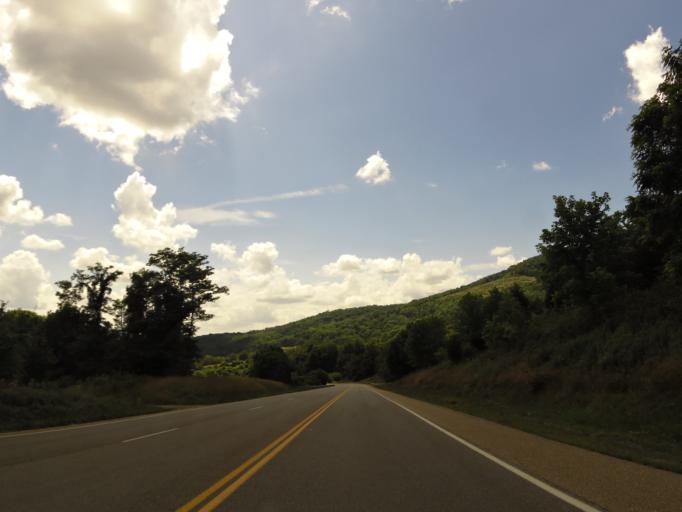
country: US
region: Virginia
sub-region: Lee County
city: Dryden
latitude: 36.7220
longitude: -82.9377
